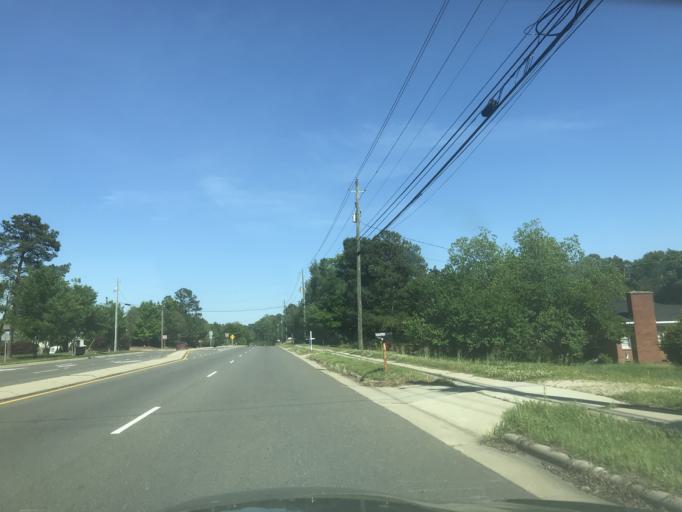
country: US
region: North Carolina
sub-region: Wake County
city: Cary
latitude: 35.7462
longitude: -78.7315
